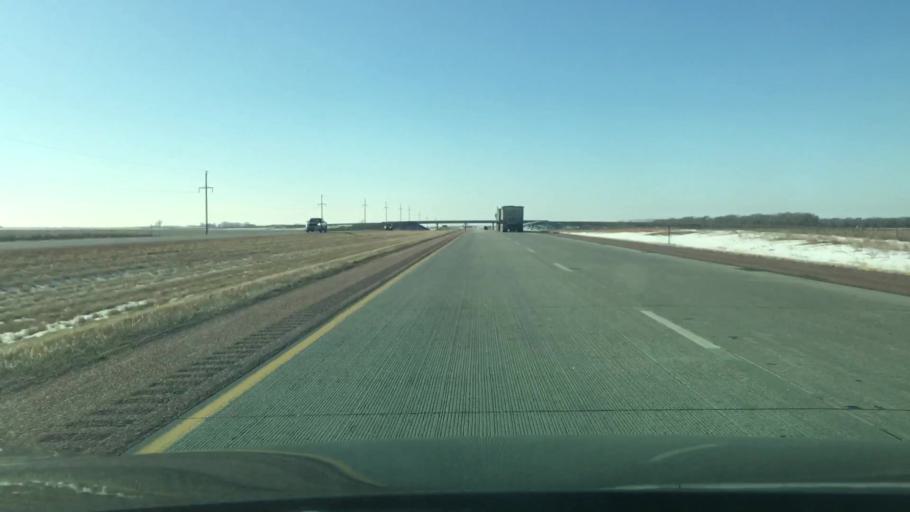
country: US
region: South Dakota
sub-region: Davison County
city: Mitchell
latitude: 43.6960
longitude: -98.1789
